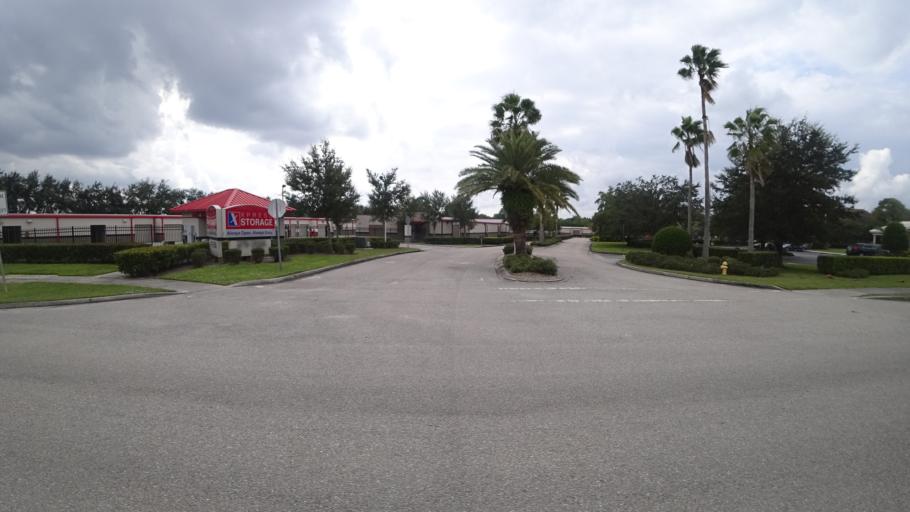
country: US
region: Florida
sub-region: Manatee County
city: Ellenton
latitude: 27.5419
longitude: -82.4768
